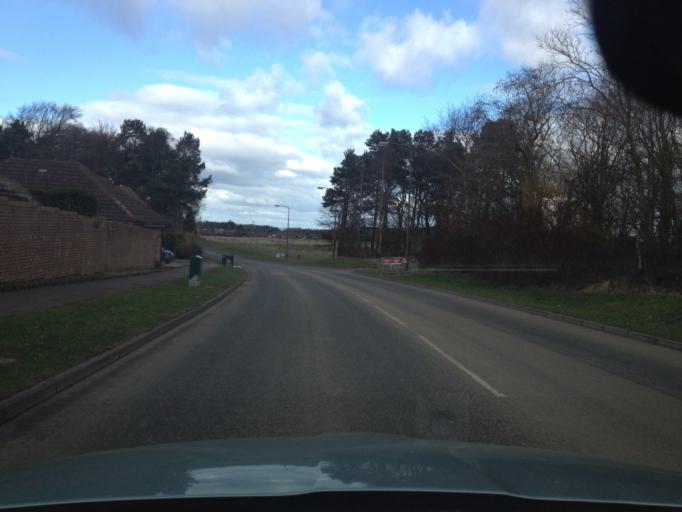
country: GB
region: Scotland
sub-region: West Lothian
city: Mid Calder
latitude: 55.8637
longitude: -3.5041
